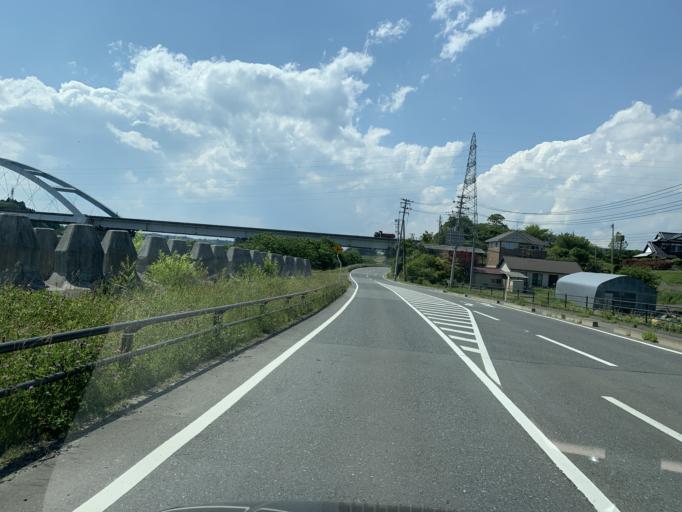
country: JP
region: Miyagi
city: Yamoto
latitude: 38.4152
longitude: 141.1455
